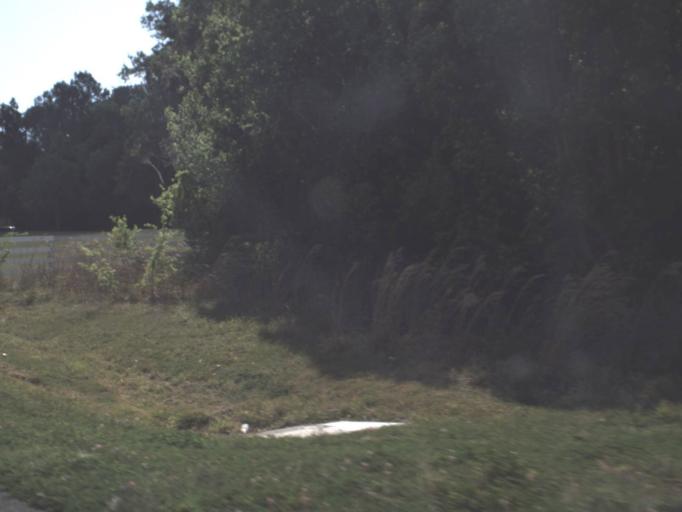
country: US
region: Florida
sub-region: Marion County
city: Dunnellon
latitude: 29.1720
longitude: -82.3329
